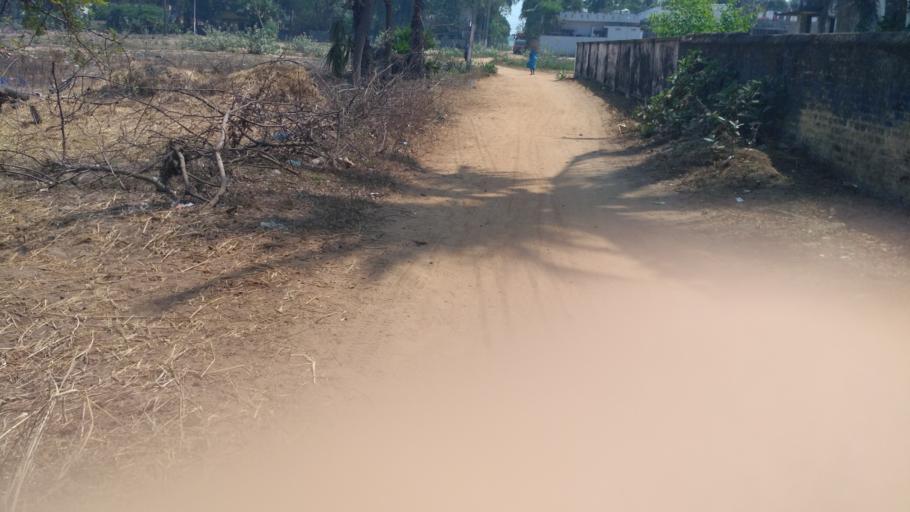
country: IN
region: Andhra Pradesh
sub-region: Prakasam
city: Chirala
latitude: 15.8263
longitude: 80.3730
